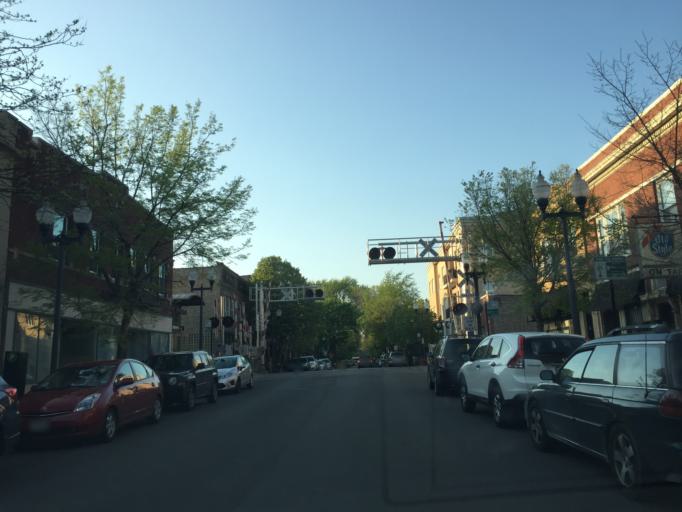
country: US
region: Illinois
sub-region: Cook County
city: Lincolnwood
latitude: 41.9659
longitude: -87.6937
